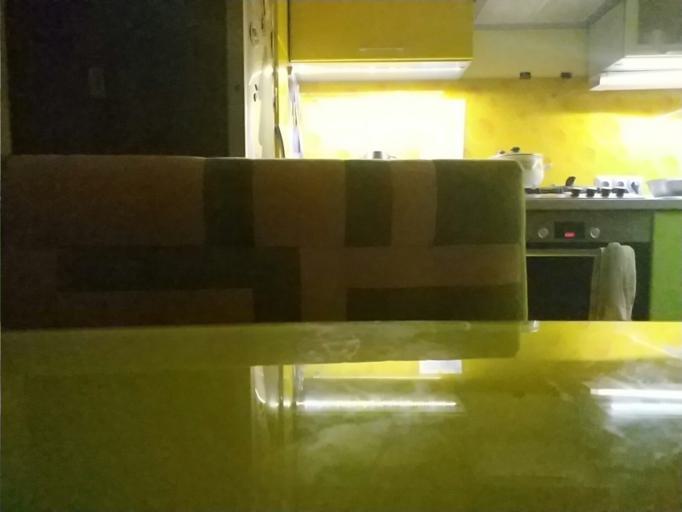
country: RU
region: Republic of Karelia
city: Pyaozerskiy
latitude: 65.8152
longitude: 30.4661
